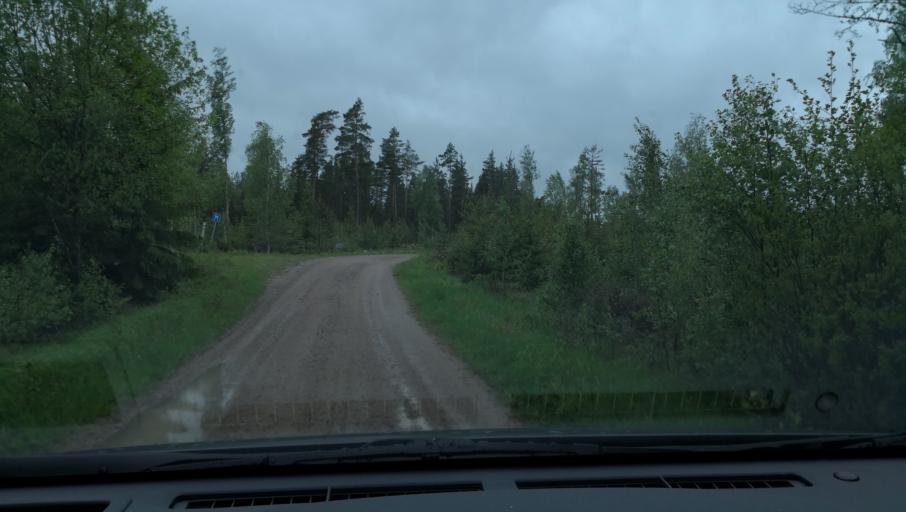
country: SE
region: Uppsala
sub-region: Enkopings Kommun
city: Orsundsbro
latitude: 59.9362
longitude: 17.3136
